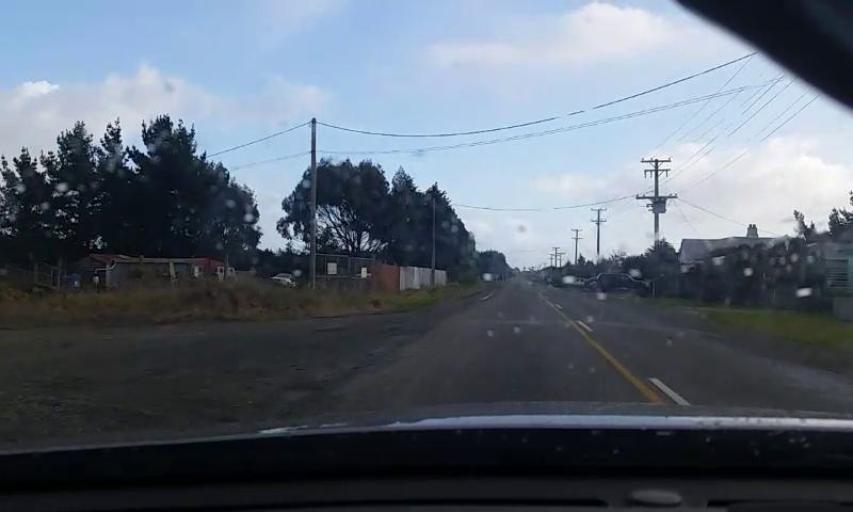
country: NZ
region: Southland
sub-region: Invercargill City
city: Invercargill
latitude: -46.3581
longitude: 168.3436
